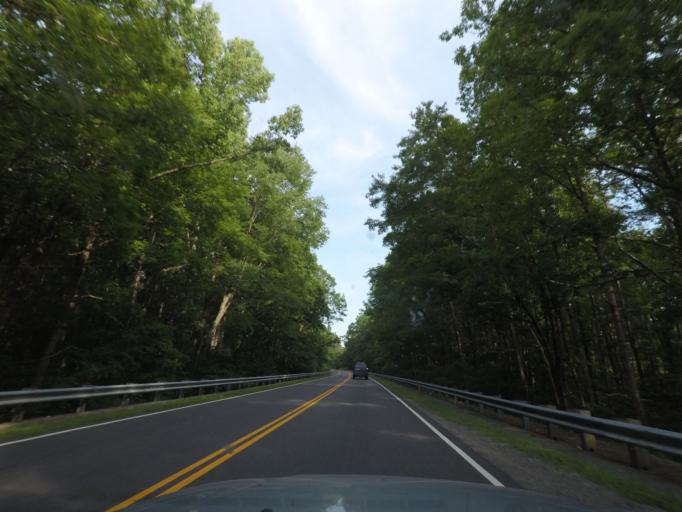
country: US
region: Virginia
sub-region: Mecklenburg County
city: Clarksville
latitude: 36.6977
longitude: -78.6272
